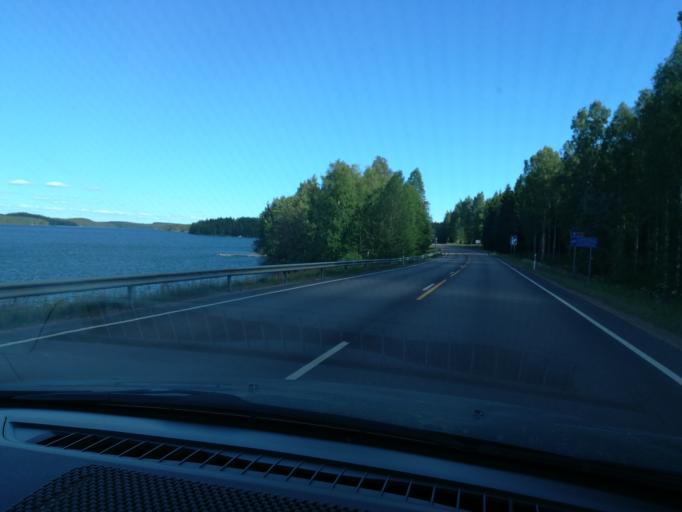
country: FI
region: Southern Savonia
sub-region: Mikkeli
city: Puumala
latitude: 61.5127
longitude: 28.1780
